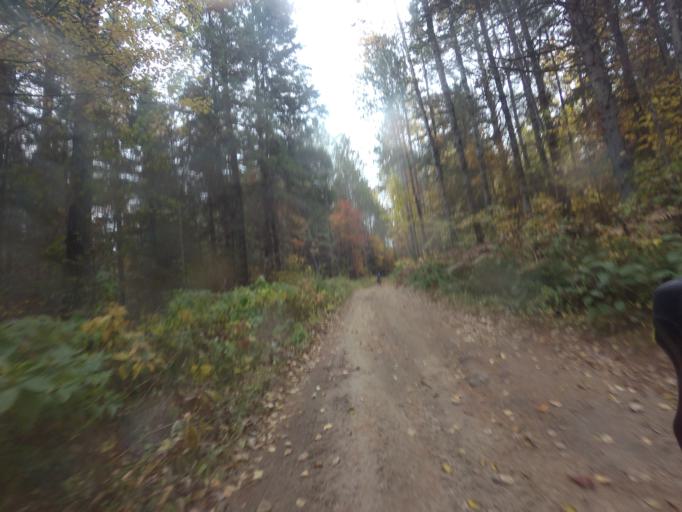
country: CA
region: Ontario
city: Petawawa
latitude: 45.7743
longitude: -77.3771
